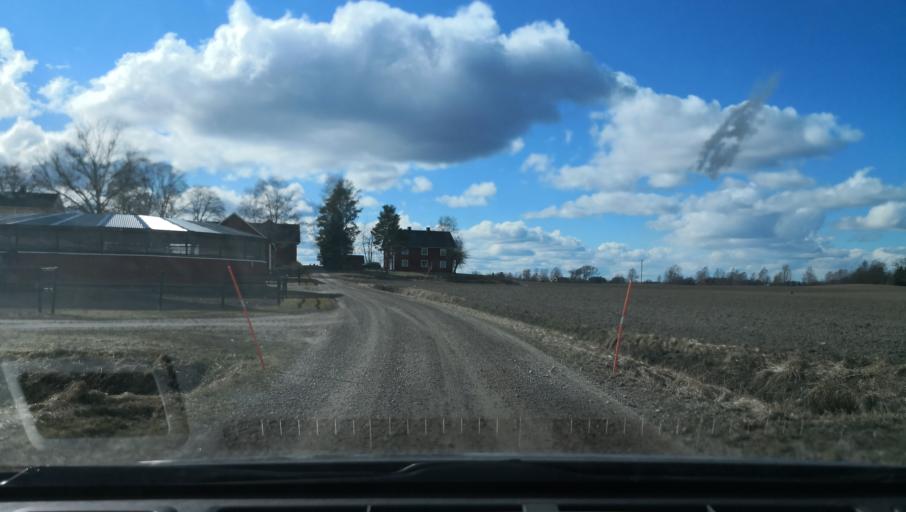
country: SE
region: OErebro
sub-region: Lindesbergs Kommun
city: Fellingsbro
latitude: 59.4141
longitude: 15.6392
